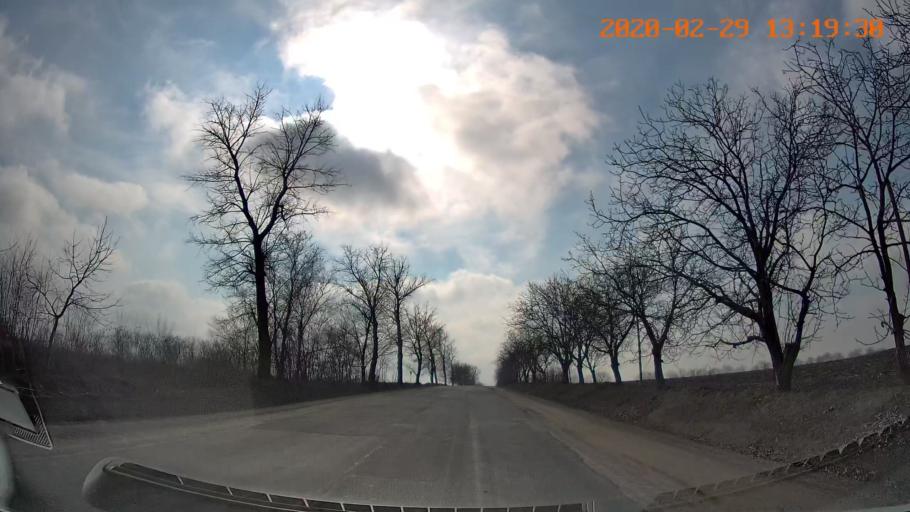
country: MD
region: Telenesti
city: Camenca
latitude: 47.9880
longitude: 28.6504
